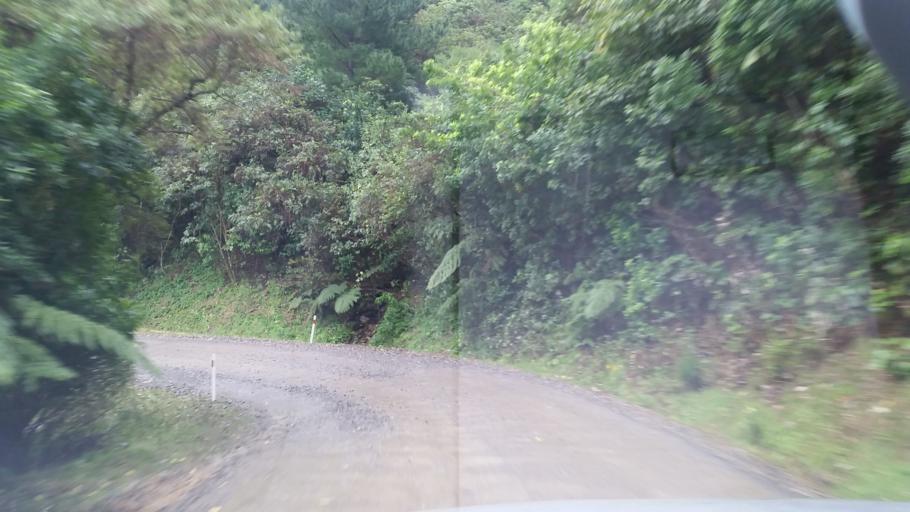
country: NZ
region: Marlborough
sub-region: Marlborough District
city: Picton
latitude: -41.1776
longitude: 174.0695
